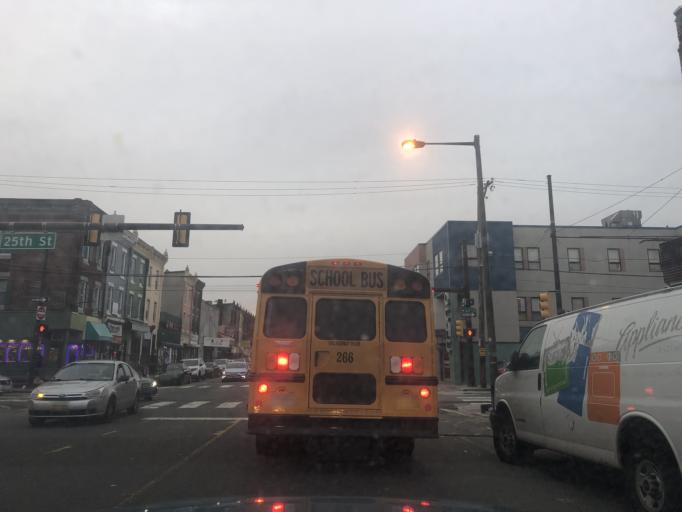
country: US
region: Pennsylvania
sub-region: Philadelphia County
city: Philadelphia
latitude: 39.9961
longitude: -75.1737
